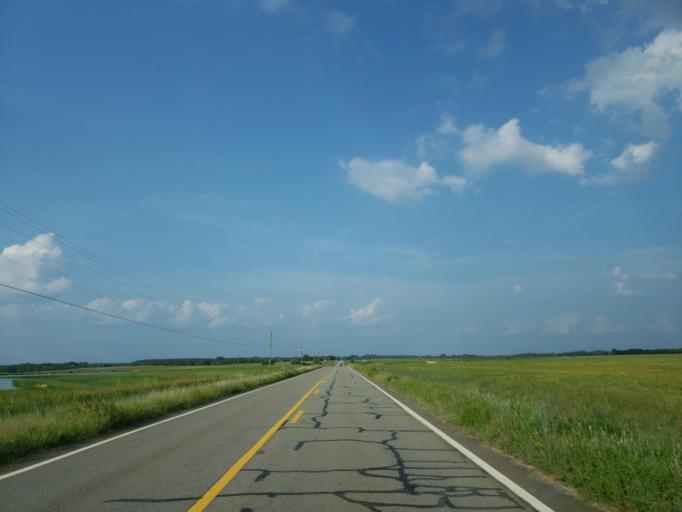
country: US
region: Alabama
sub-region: Greene County
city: Eutaw
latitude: 32.8063
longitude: -87.9532
